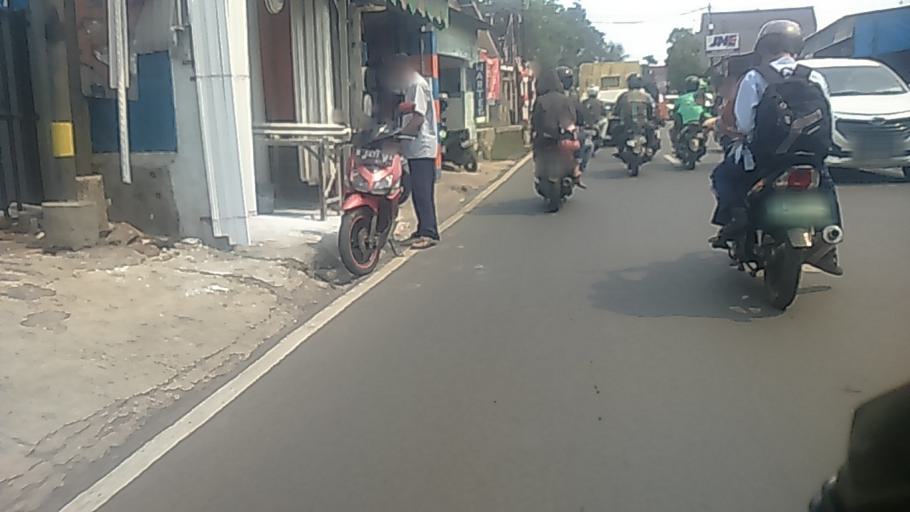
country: ID
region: West Java
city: Depok
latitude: -6.3408
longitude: 106.8047
